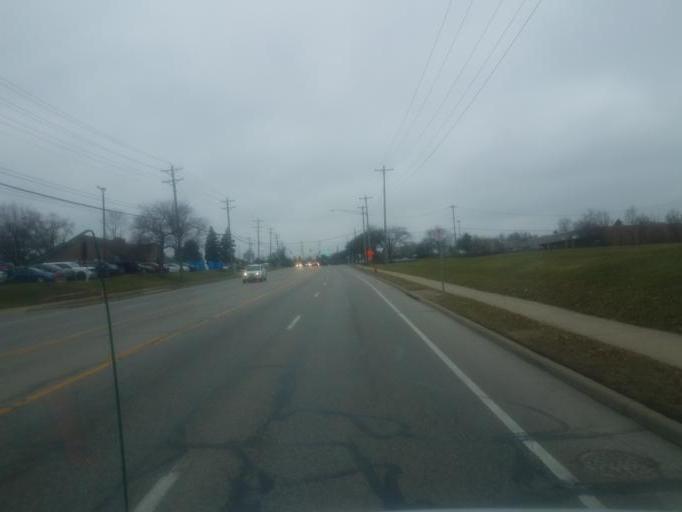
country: US
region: Ohio
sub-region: Franklin County
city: Westerville
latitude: 40.1107
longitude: -82.9440
